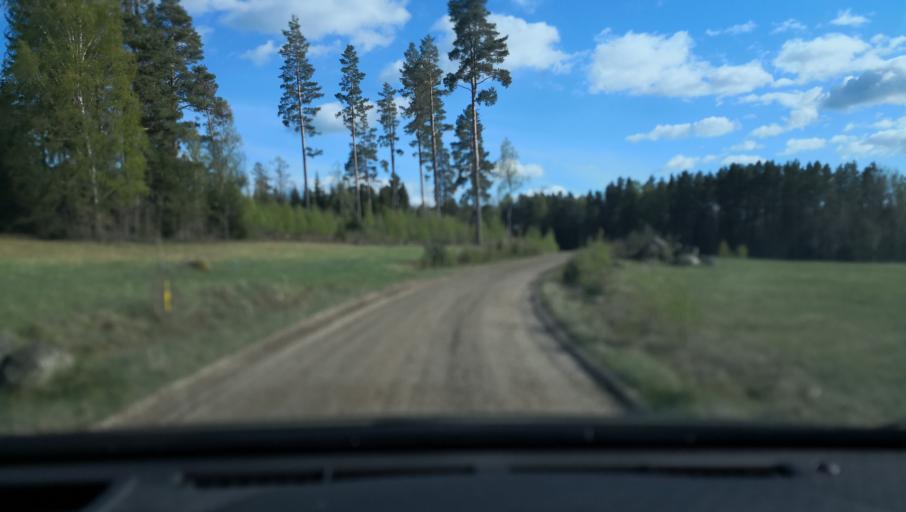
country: SE
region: OErebro
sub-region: Askersunds Kommun
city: Asbro
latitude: 58.8954
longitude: 15.1082
